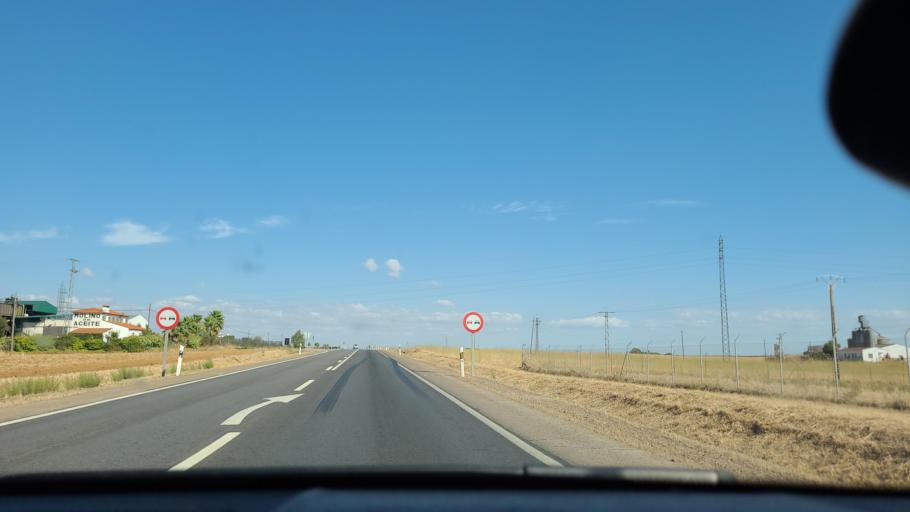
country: ES
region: Extremadura
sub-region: Provincia de Badajoz
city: Puebla de Sancho Perez
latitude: 38.4098
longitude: -6.3906
